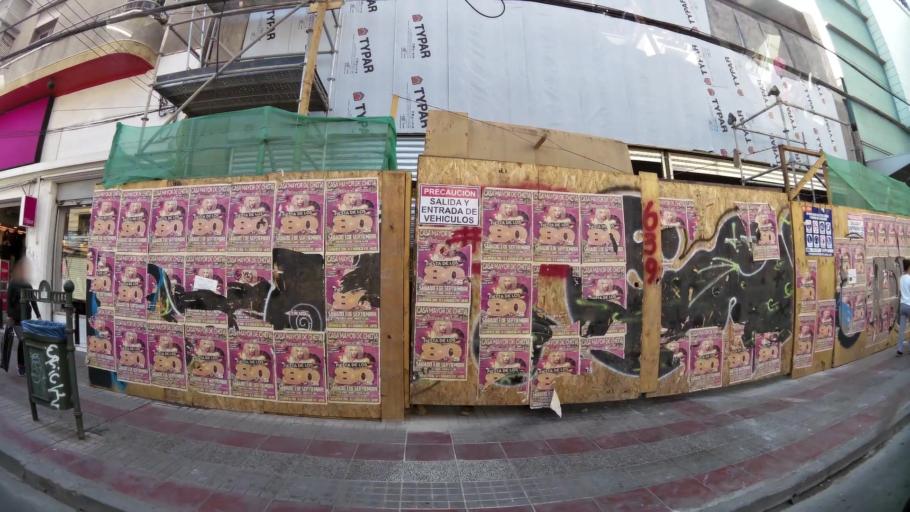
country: CL
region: Santiago Metropolitan
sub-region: Provincia de Maipo
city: San Bernardo
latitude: -33.5950
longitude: -70.7061
